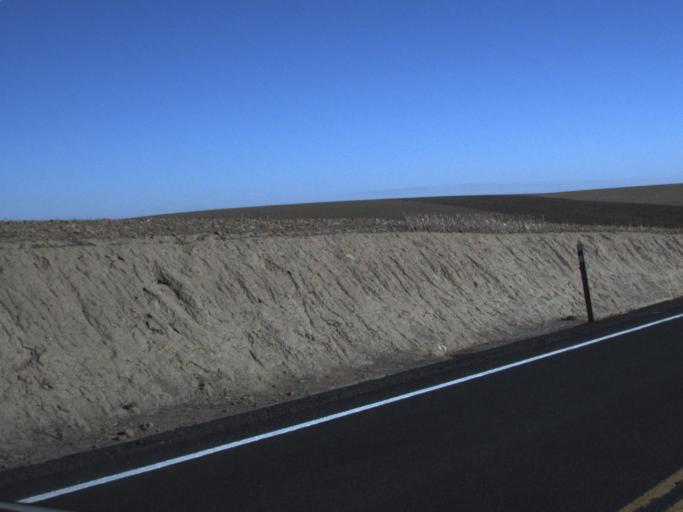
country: US
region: Washington
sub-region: Adams County
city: Ritzville
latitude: 47.0075
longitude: -118.3501
